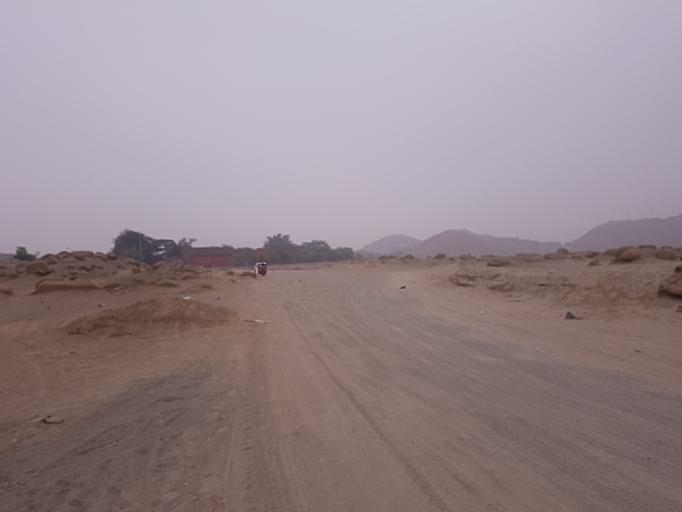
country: PE
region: Lima
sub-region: Lima
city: Santa Maria
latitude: -11.9862
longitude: -76.9125
